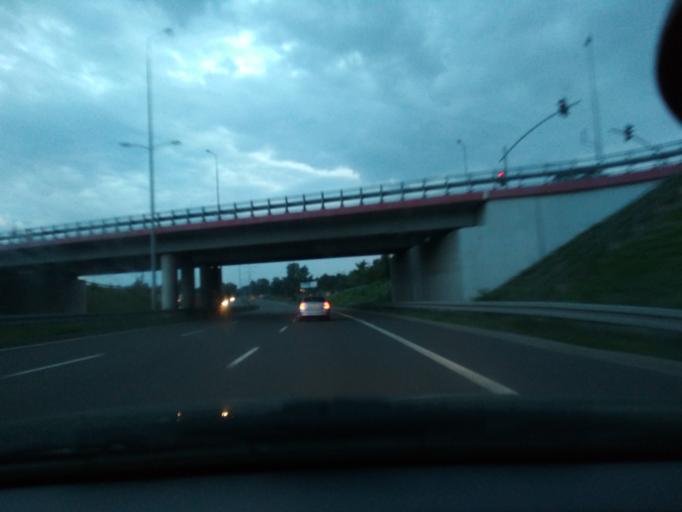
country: PL
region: Silesian Voivodeship
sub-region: Ruda Slaska
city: Ruda Slaska
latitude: 50.2974
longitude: 18.8330
